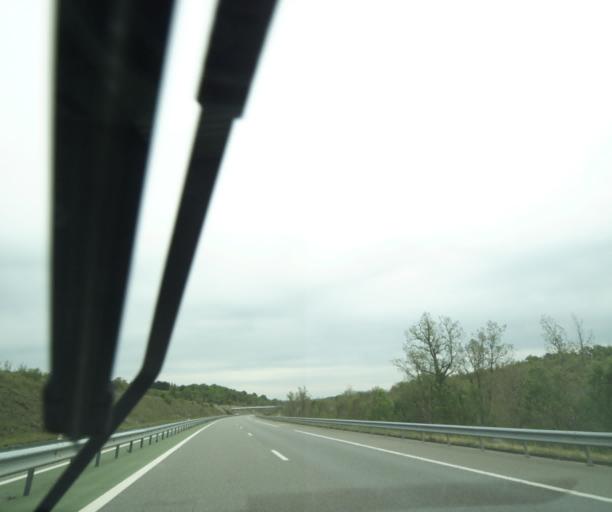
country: FR
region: Midi-Pyrenees
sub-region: Departement du Lot
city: Lalbenque
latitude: 44.3687
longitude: 1.4986
